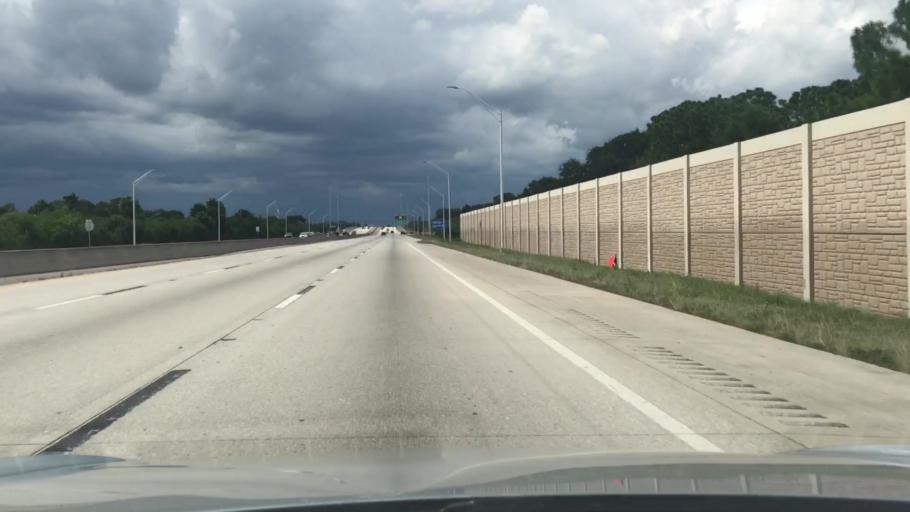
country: US
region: Florida
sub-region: Brevard County
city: Cocoa West
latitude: 28.3536
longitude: -80.7898
